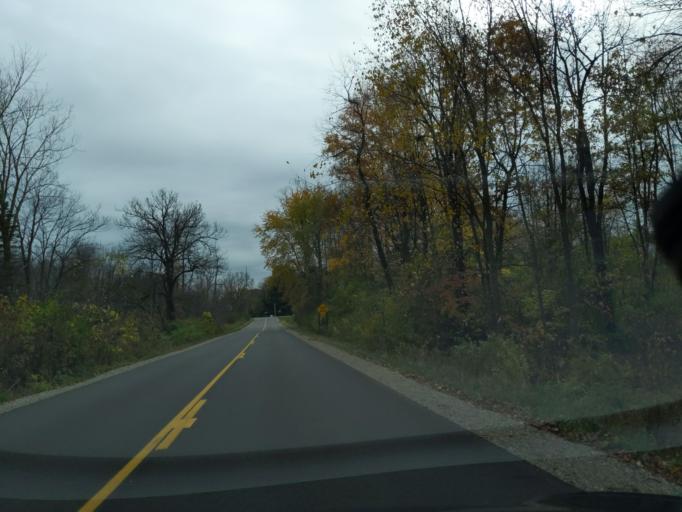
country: US
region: Michigan
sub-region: Eaton County
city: Eaton Rapids
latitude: 42.5261
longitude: -84.6211
